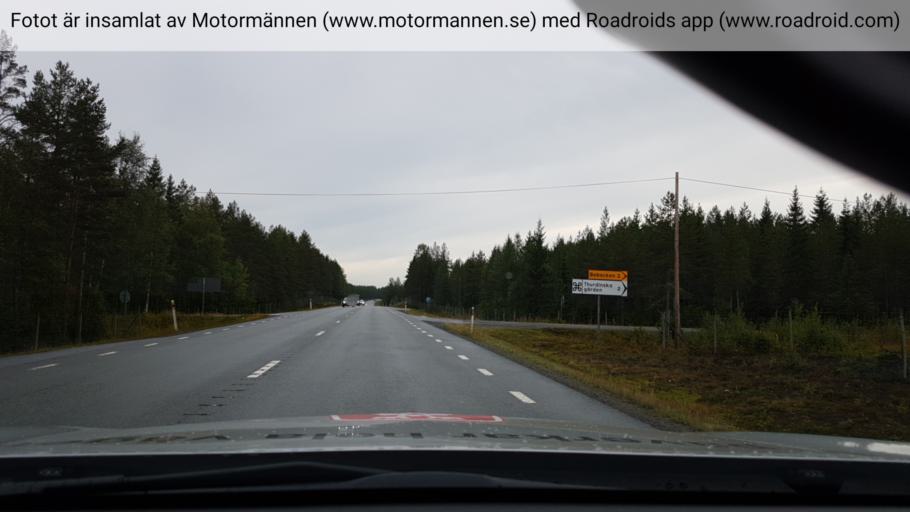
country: SE
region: Vaesterbotten
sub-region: Robertsfors Kommun
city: Robertsfors
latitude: 64.0528
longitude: 20.8481
